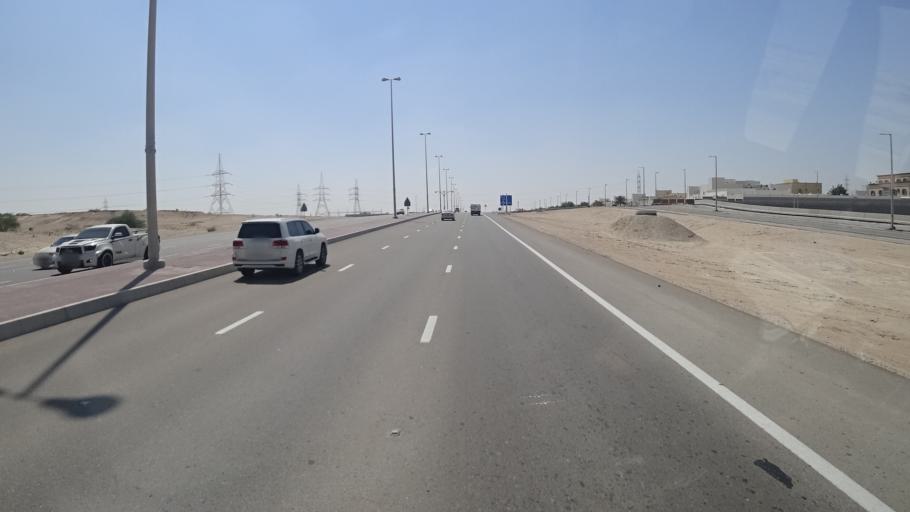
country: AE
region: Abu Dhabi
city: Abu Dhabi
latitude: 24.3001
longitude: 54.6652
